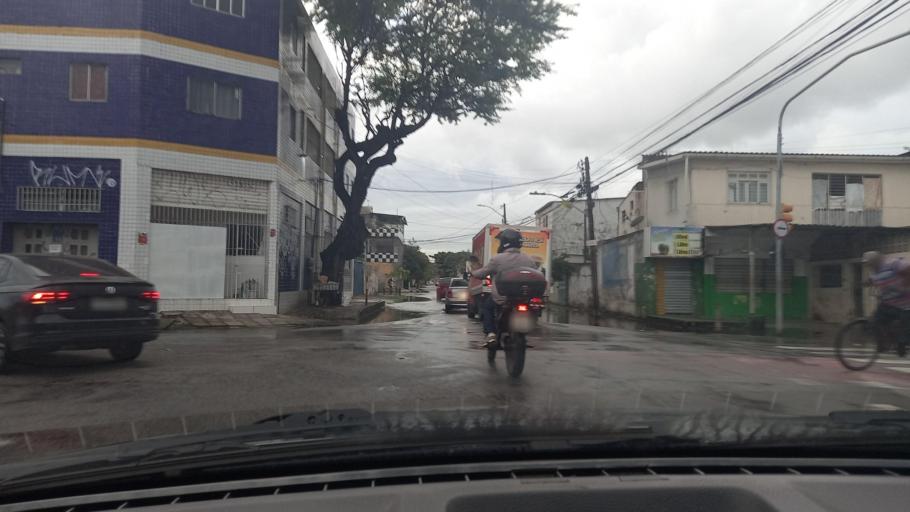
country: ET
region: Gambela
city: Gambela
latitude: 8.1069
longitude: 34.9258
